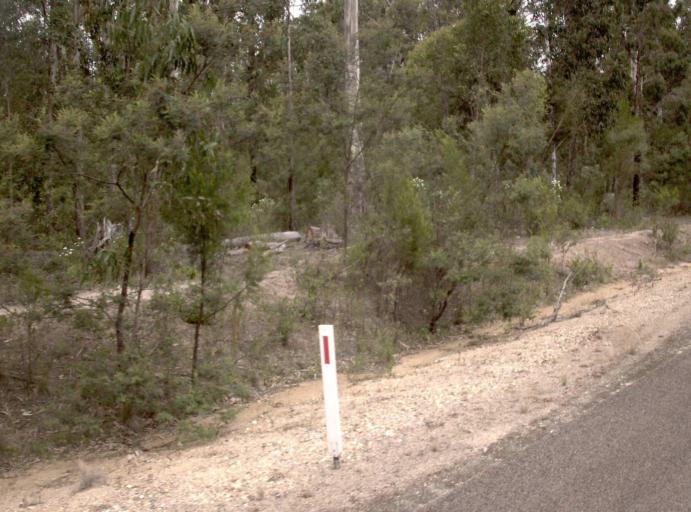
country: AU
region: Victoria
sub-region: East Gippsland
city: Lakes Entrance
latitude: -37.7080
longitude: 148.0696
